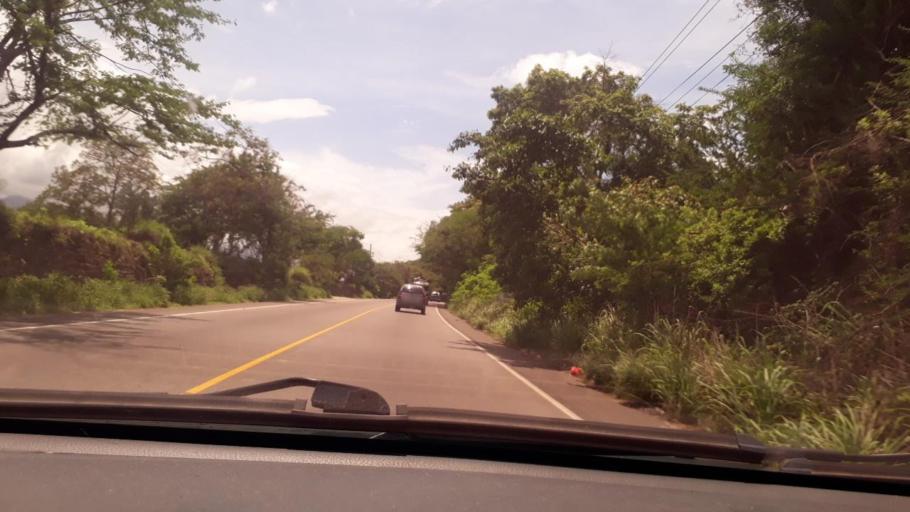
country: GT
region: Zacapa
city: Rio Hondo
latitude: 15.0528
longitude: -89.5617
